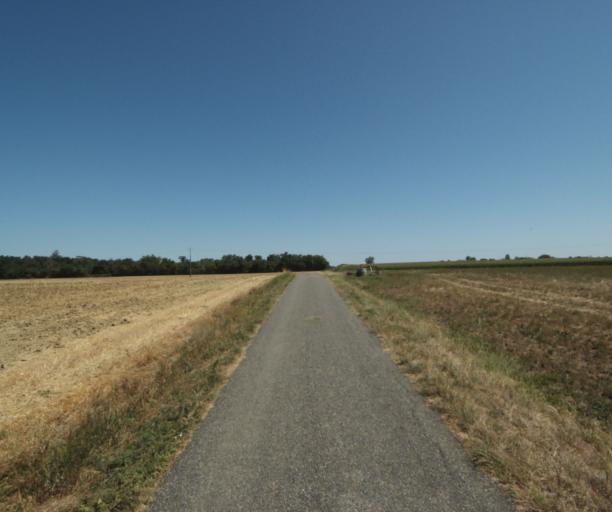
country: FR
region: Midi-Pyrenees
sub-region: Departement de la Haute-Garonne
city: Revel
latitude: 43.4768
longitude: 1.9678
